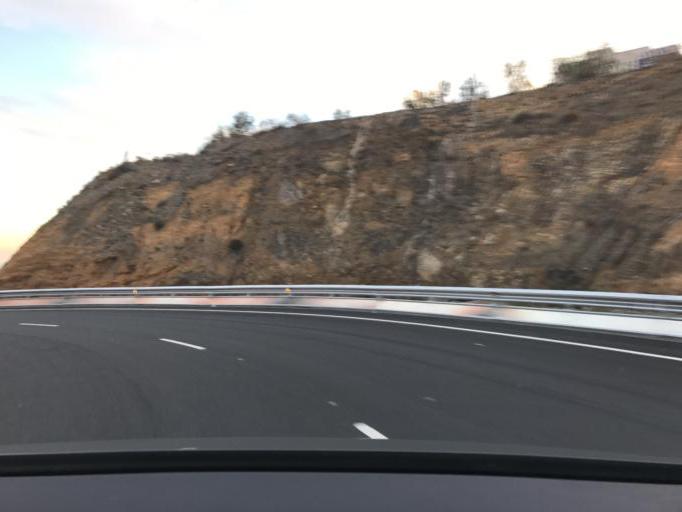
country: ES
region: Andalusia
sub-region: Provincia de Almeria
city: Aguadulce
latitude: 36.8260
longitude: -2.5834
